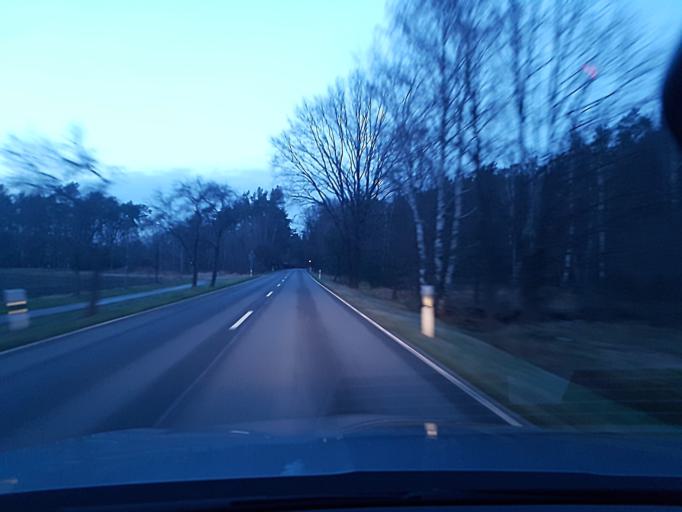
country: DE
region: Brandenburg
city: Ruckersdorf
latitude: 51.5875
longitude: 13.5617
